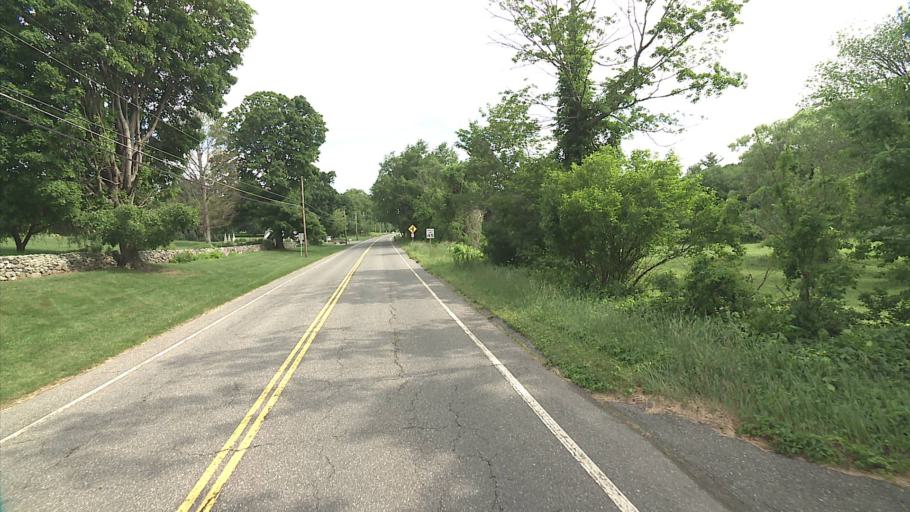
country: US
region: Connecticut
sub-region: Litchfield County
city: Litchfield
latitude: 41.6979
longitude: -73.1835
